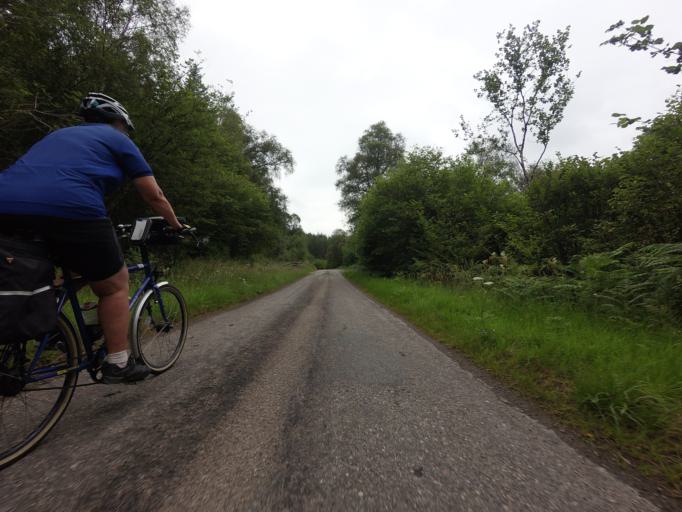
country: GB
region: Scotland
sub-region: Highland
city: Evanton
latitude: 57.9633
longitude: -4.4089
